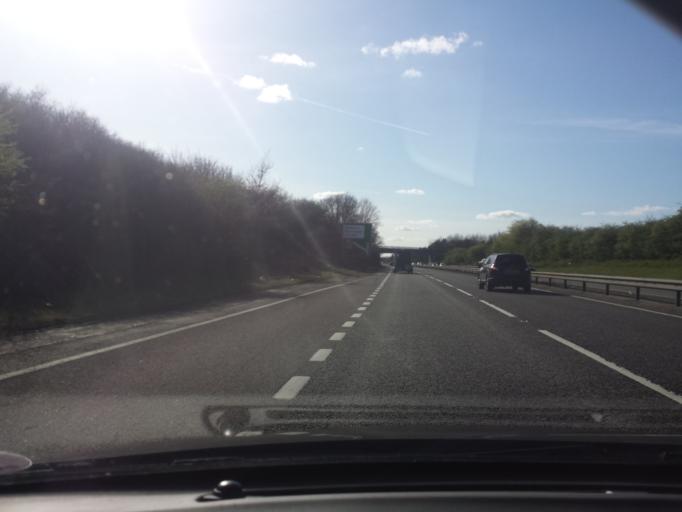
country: GB
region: England
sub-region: Essex
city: Colchester
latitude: 51.9253
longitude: 0.9208
